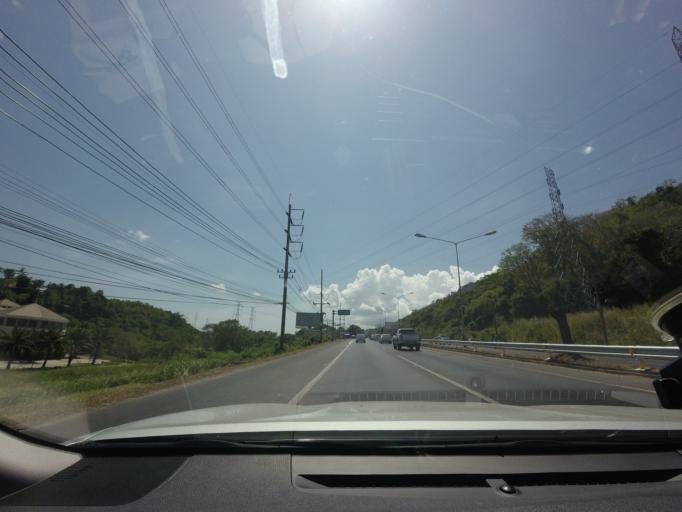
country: TH
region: Phuket
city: Ban Ko Kaeo
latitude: 7.9448
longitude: 98.3832
